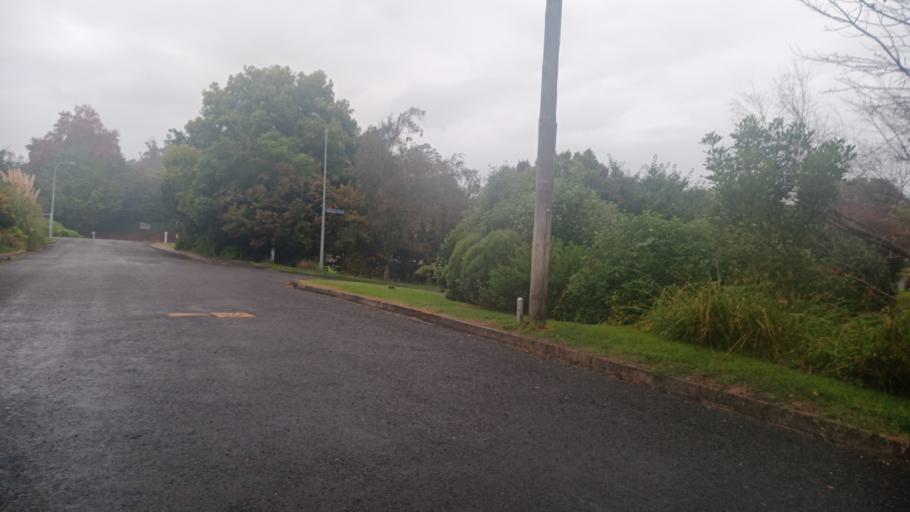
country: NZ
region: Gisborne
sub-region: Gisborne District
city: Gisborne
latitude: -38.6555
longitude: 178.0358
